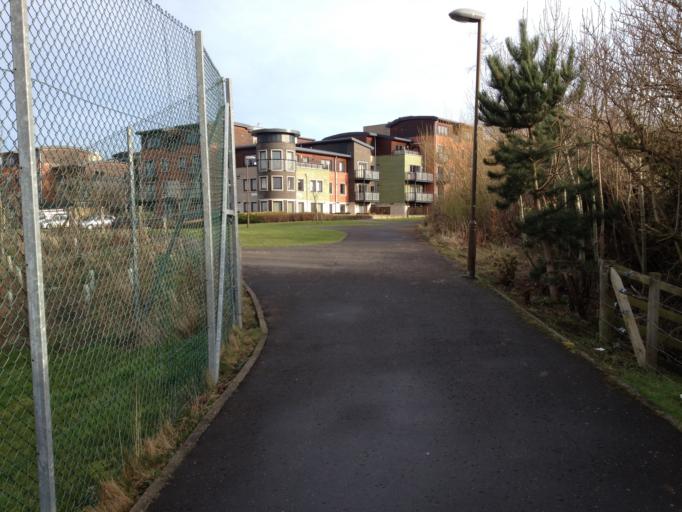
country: GB
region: Scotland
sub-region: Edinburgh
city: Colinton
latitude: 55.9258
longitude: -3.2399
